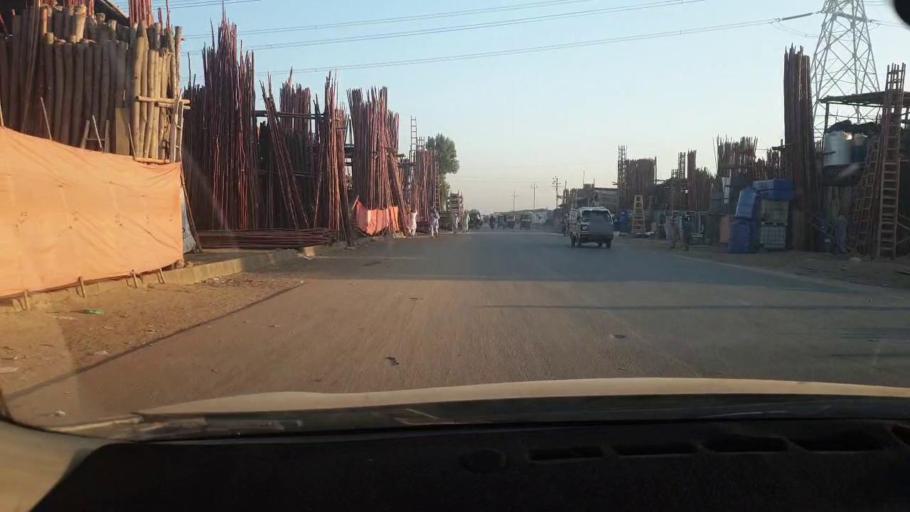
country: PK
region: Sindh
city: Malir Cantonment
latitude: 24.9957
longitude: 67.1424
